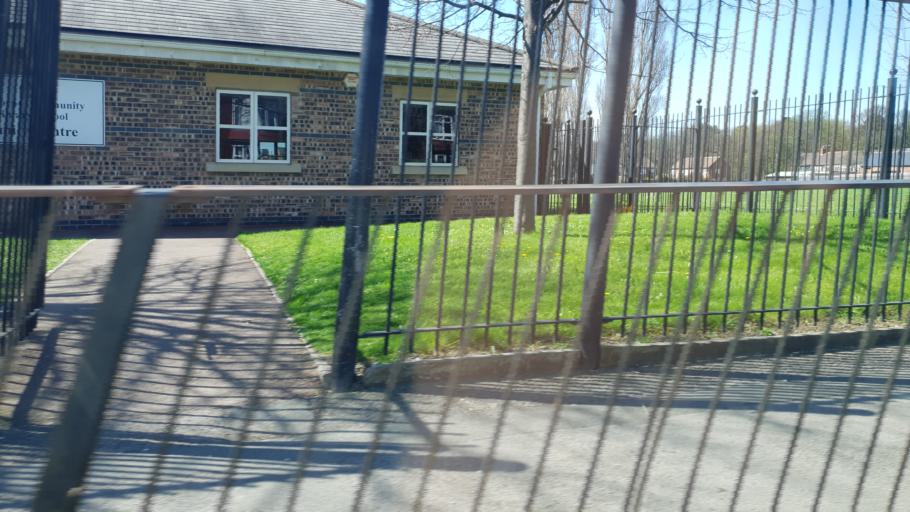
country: GB
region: England
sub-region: Middlesbrough
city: Middlesbrough
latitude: 54.5593
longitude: -1.2483
